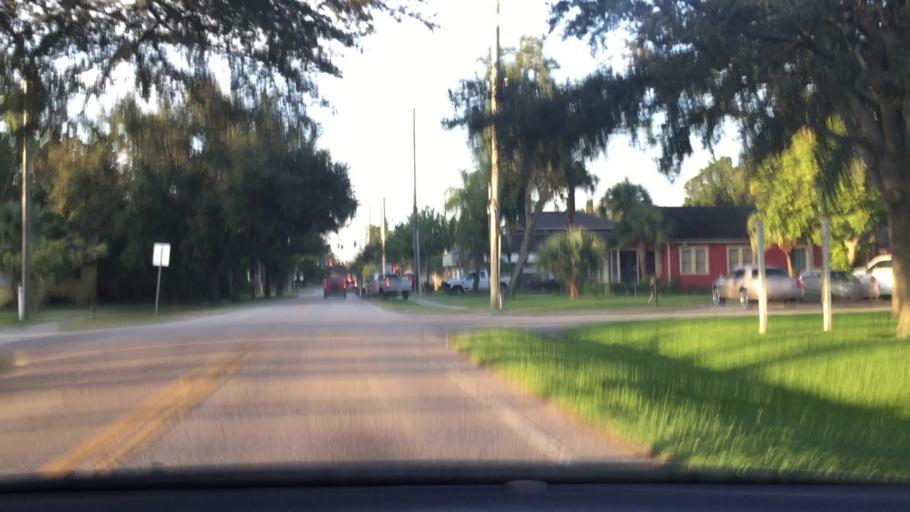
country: US
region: Florida
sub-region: Orange County
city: Fairview Shores
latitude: 28.5730
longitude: -81.4019
